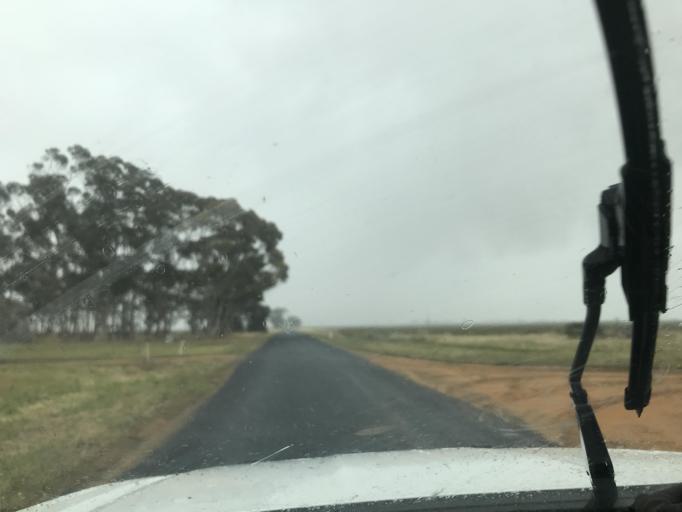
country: AU
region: South Australia
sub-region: Tatiara
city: Bordertown
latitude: -36.3154
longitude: 141.1690
